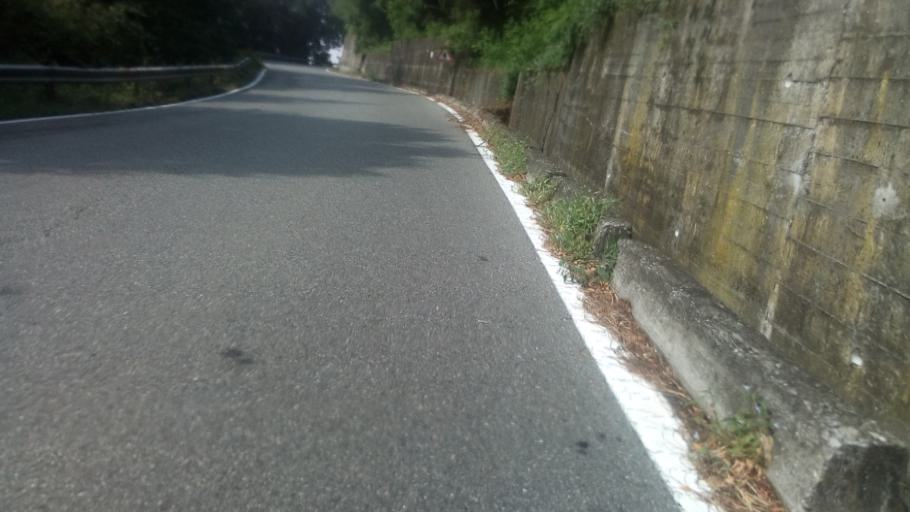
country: IT
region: Piedmont
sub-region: Provincia di Torino
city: Strambinello
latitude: 45.4228
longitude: 7.7643
